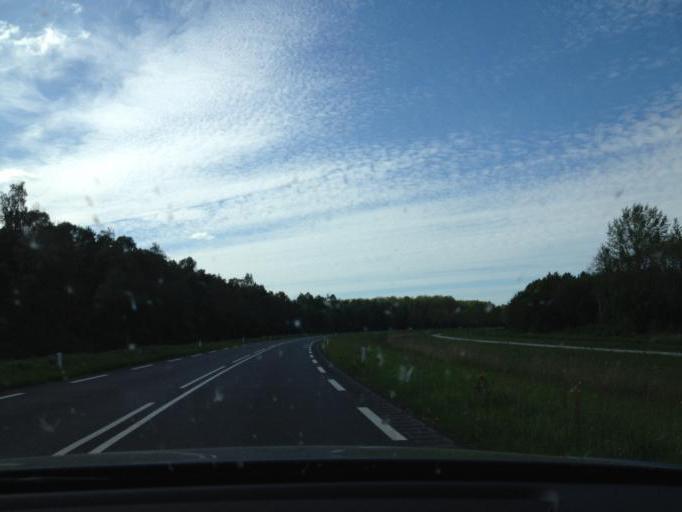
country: NL
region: Gelderland
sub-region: Gemeente Nijkerk
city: Nijkerk
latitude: 52.2645
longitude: 5.4564
